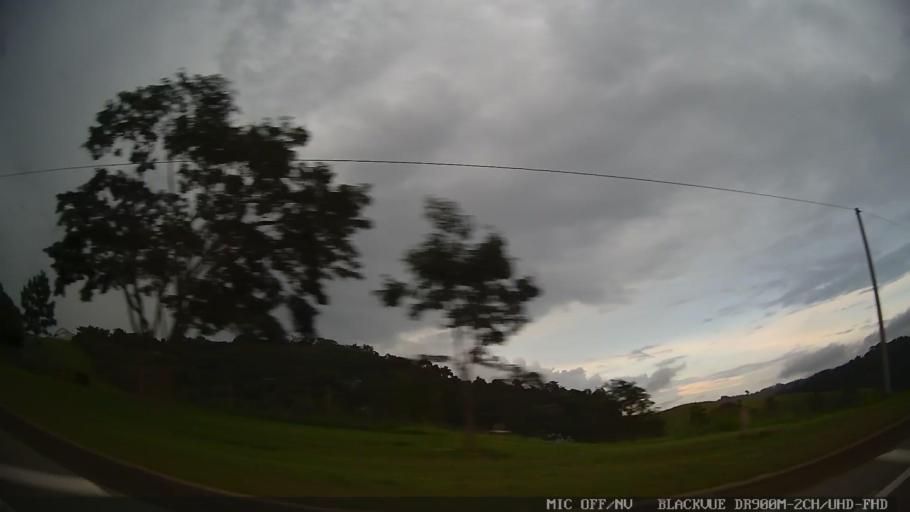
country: BR
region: Sao Paulo
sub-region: Caraguatatuba
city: Caraguatatuba
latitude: -23.4384
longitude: -45.6139
